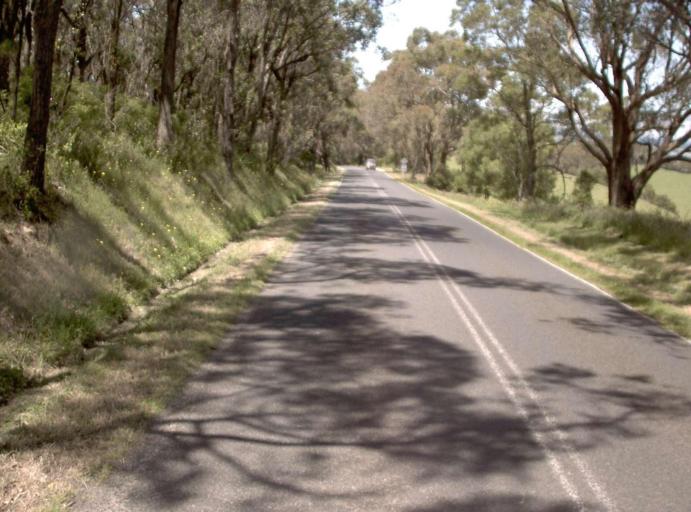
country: AU
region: Victoria
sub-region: Bass Coast
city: North Wonthaggi
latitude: -38.7399
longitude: 146.1286
